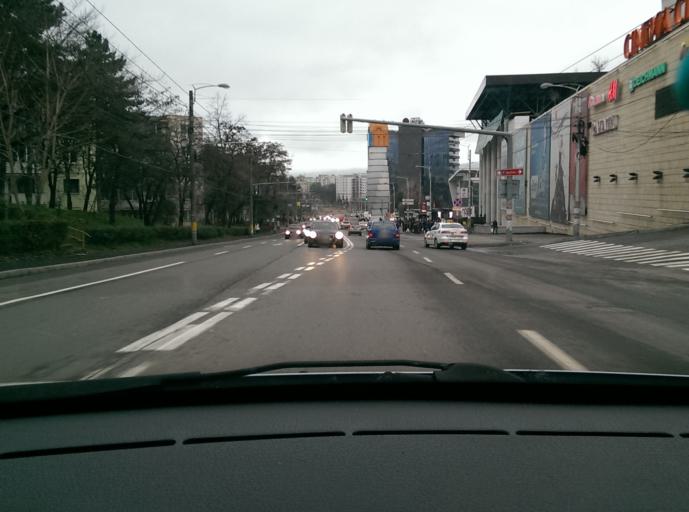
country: RO
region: Cluj
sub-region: Municipiul Cluj-Napoca
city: Cluj-Napoca
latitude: 46.7708
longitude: 23.6269
